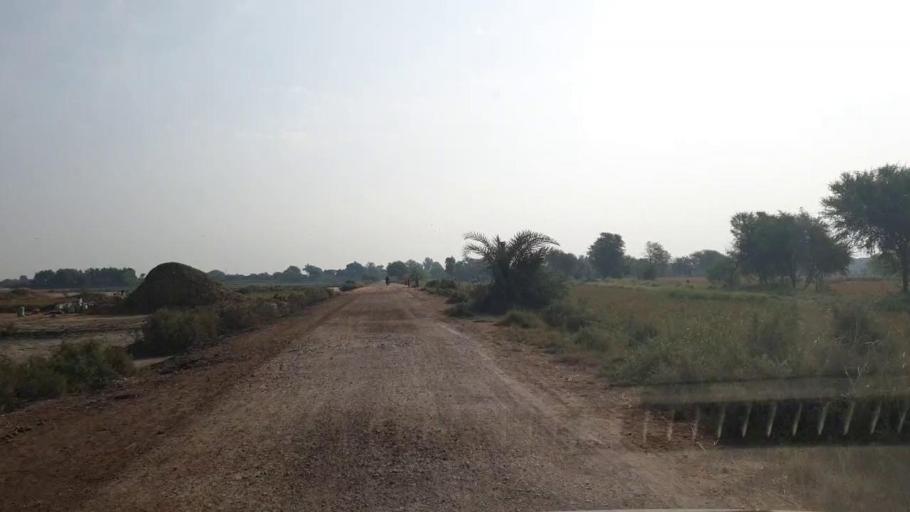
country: PK
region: Sindh
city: Talhar
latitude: 24.8965
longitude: 68.8820
